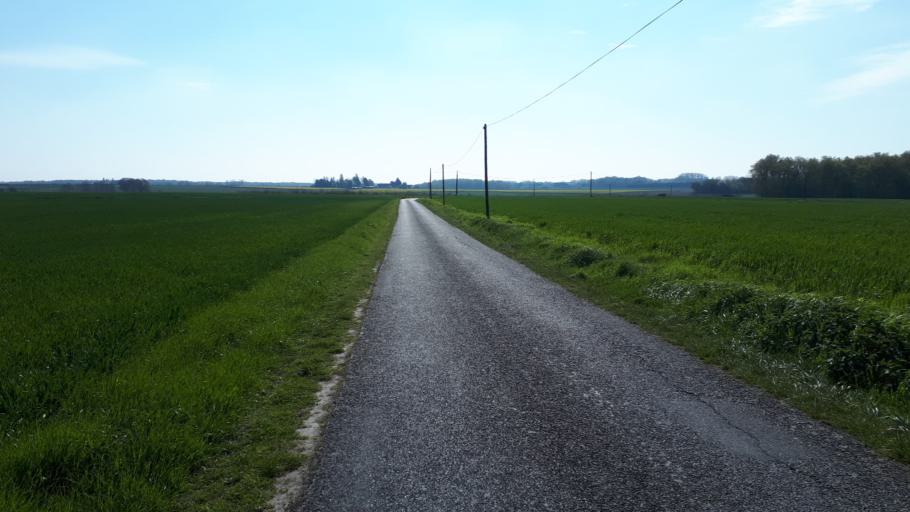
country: FR
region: Centre
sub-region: Departement du Loir-et-Cher
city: Saint-Romain-sur-Cher
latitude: 47.3763
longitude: 1.3847
